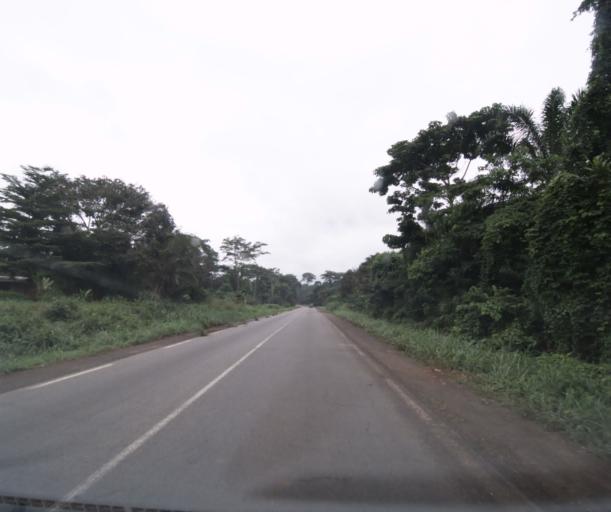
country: CM
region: Centre
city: Eseka
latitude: 3.8497
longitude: 10.4869
